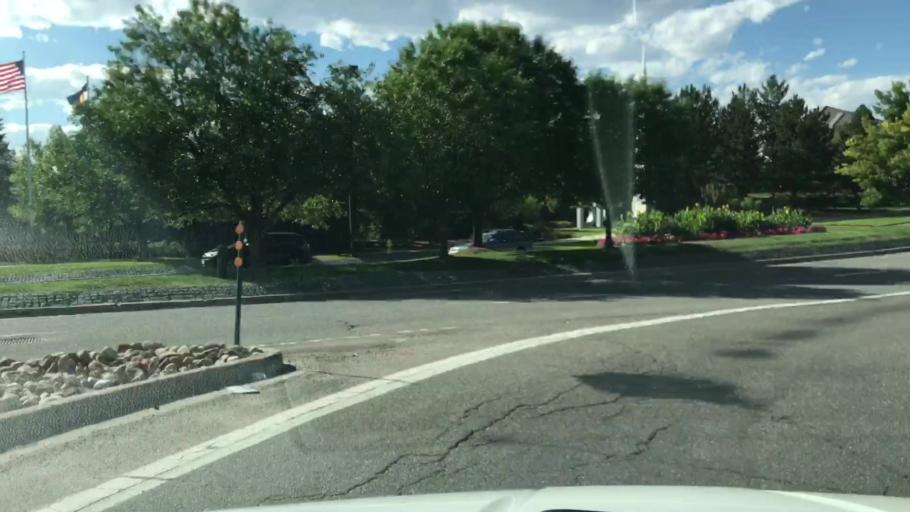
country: US
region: Colorado
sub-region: Arapahoe County
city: Greenwood Village
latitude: 39.6243
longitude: -104.9116
